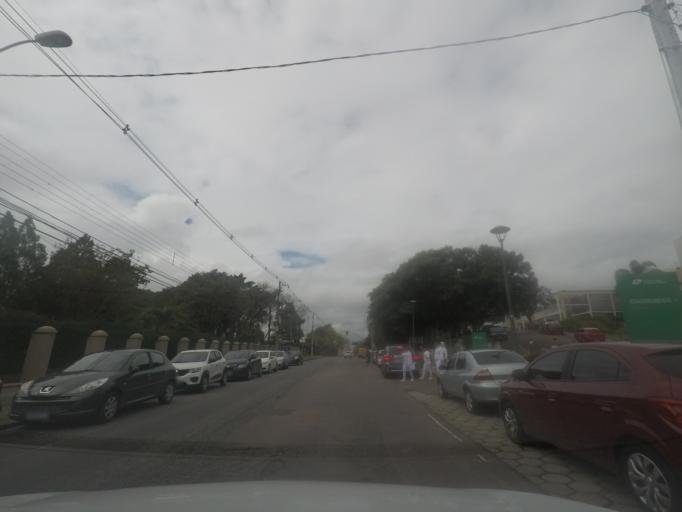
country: BR
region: Parana
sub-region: Curitiba
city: Curitiba
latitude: -25.4355
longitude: -49.2466
